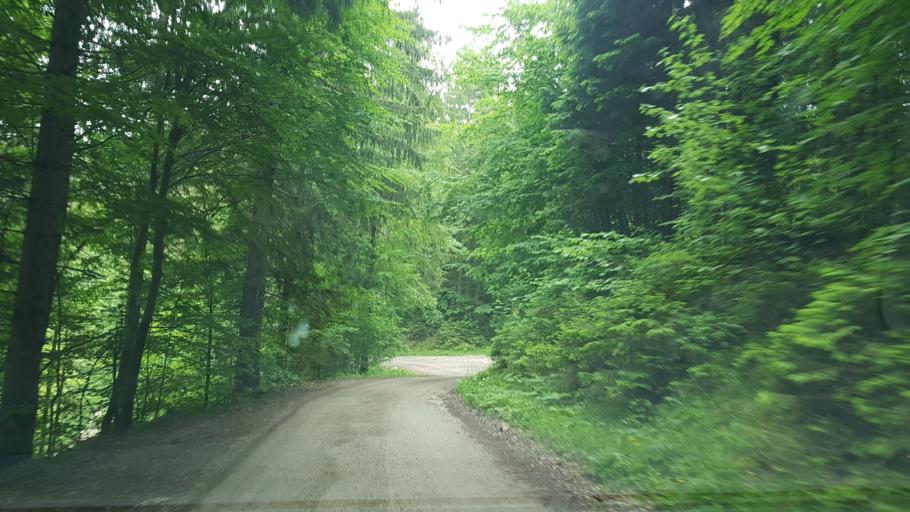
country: SI
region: Dobrna
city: Dobrna
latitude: 46.3824
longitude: 15.2268
